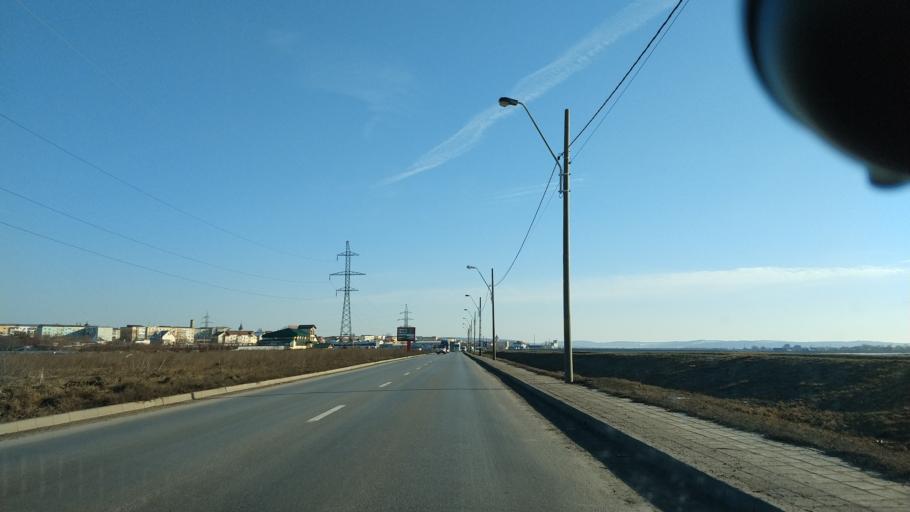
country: RO
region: Neamt
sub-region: Municipiul Roman
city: Roman
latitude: 46.9220
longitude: 26.9131
